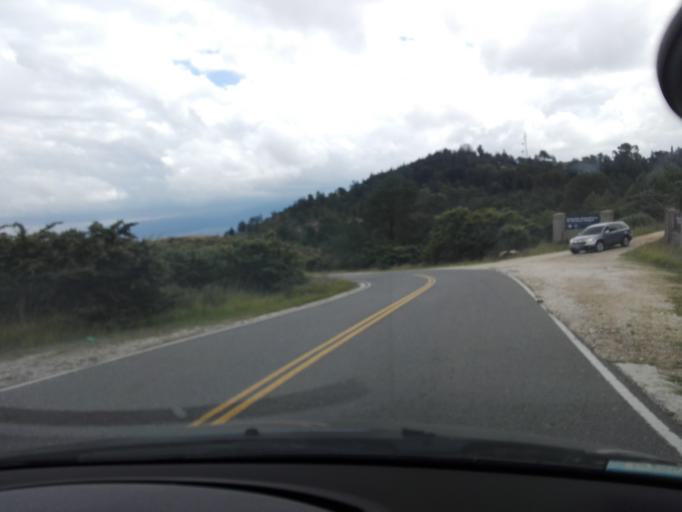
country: AR
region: Cordoba
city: Cuesta Blanca
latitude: -31.5966
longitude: -64.5431
